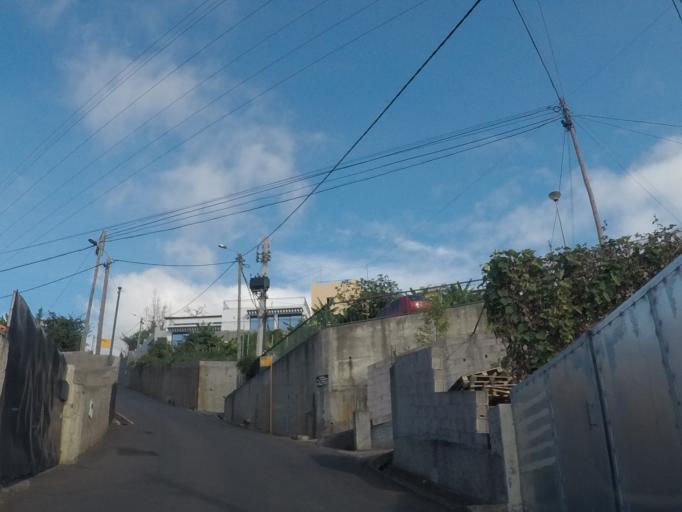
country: PT
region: Madeira
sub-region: Funchal
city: Nossa Senhora do Monte
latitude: 32.6645
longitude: -16.8864
